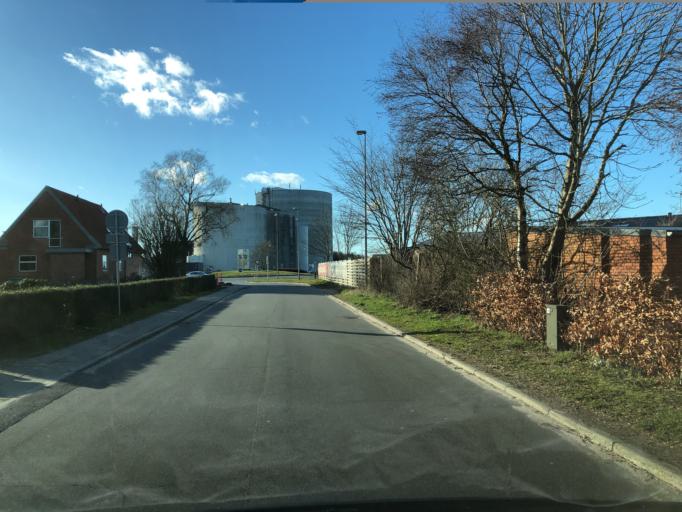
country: DK
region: Central Jutland
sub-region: Viborg Kommune
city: Karup
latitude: 56.3072
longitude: 9.1624
